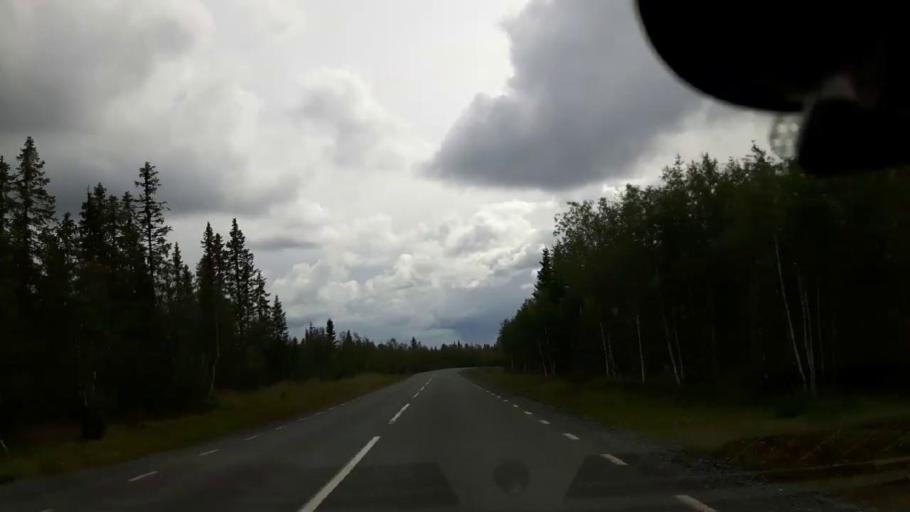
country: SE
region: Jaemtland
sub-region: Krokoms Kommun
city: Valla
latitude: 63.4570
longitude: 13.8285
